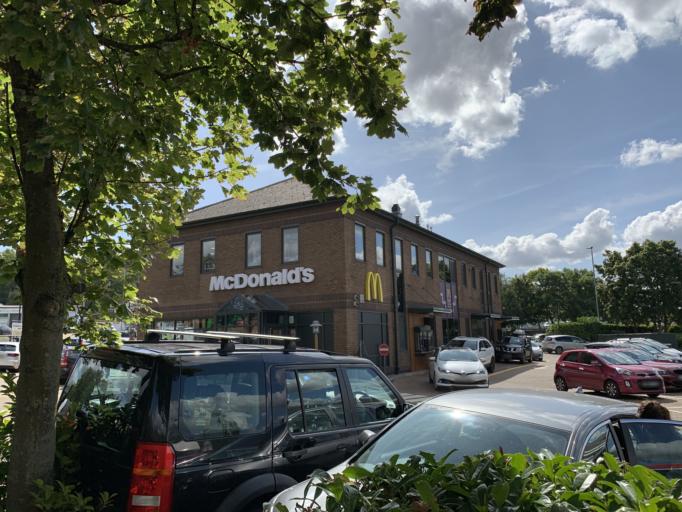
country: GB
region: England
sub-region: Kent
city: Pembury
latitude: 51.1566
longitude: 0.2898
